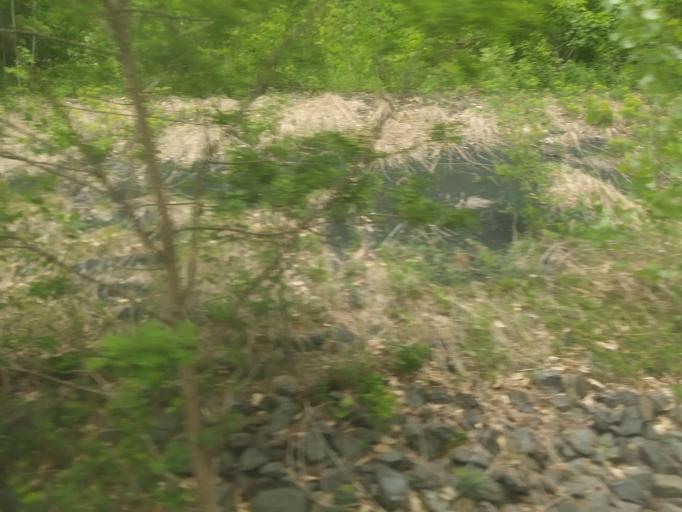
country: US
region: Massachusetts
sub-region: Franklin County
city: Buckland
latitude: 42.5759
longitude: -72.8115
